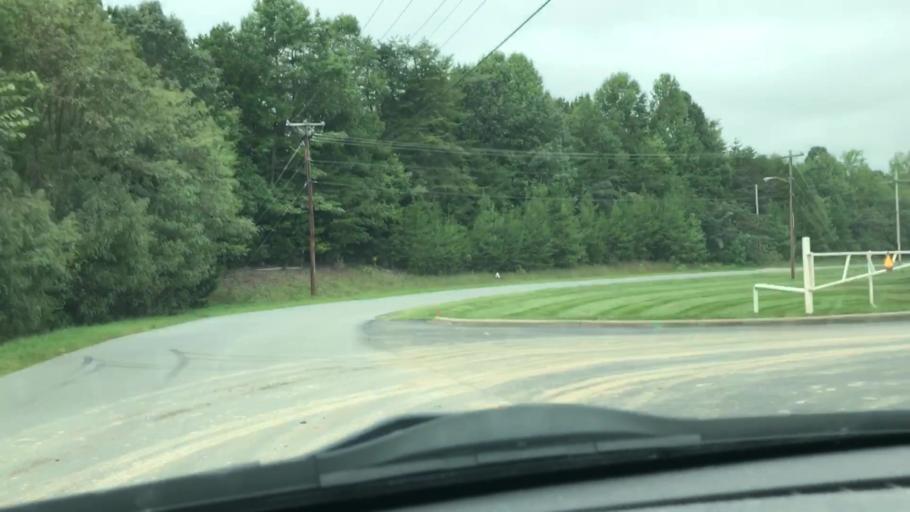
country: US
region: North Carolina
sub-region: Randolph County
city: Randleman
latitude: 35.8036
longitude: -79.8122
